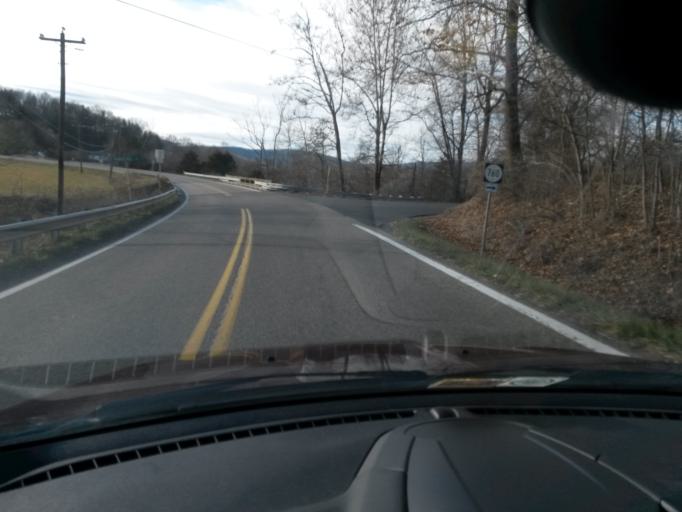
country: US
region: Virginia
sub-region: Augusta County
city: Verona
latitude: 38.2936
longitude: -79.1249
